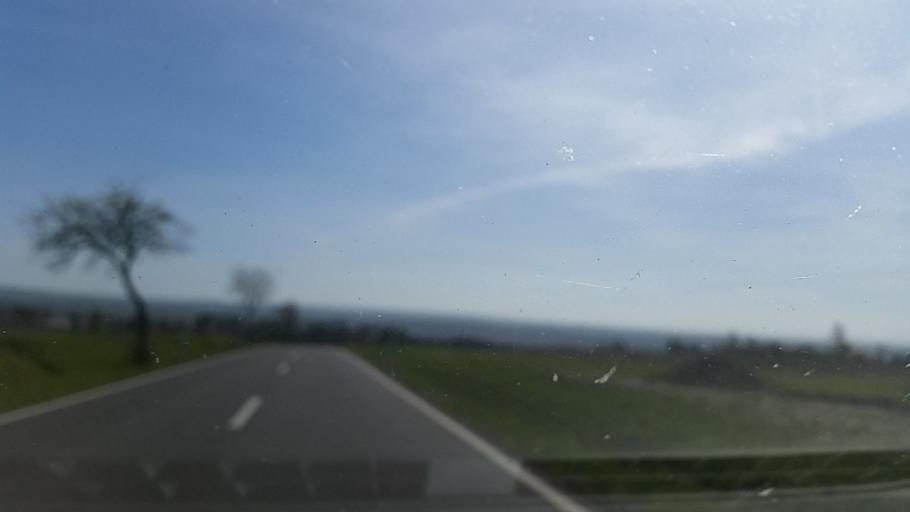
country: DE
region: Lower Saxony
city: Schoningen
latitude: 52.1451
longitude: 10.9431
